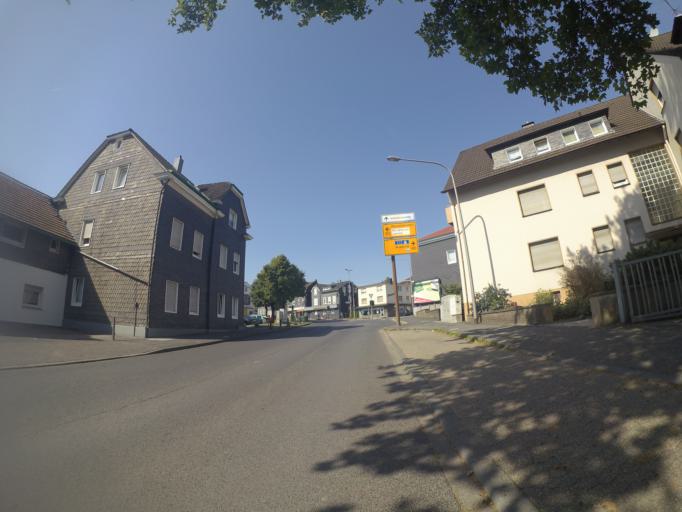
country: DE
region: North Rhine-Westphalia
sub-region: Regierungsbezirk Dusseldorf
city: Remscheid
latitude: 51.2143
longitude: 7.2417
